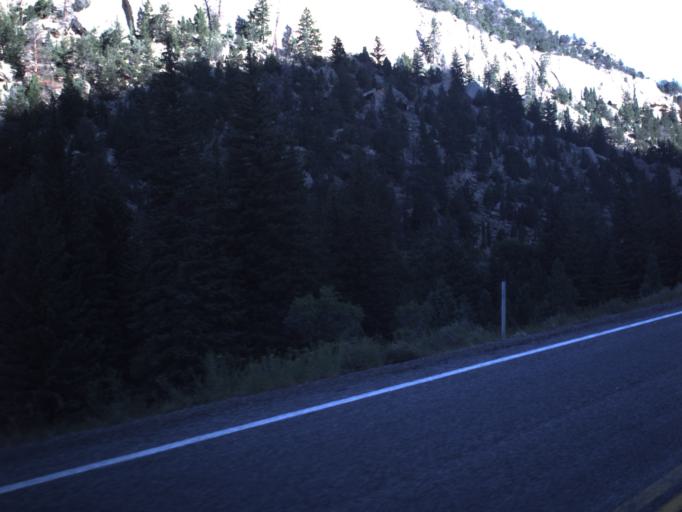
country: US
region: Utah
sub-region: Emery County
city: Huntington
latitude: 39.4273
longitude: -111.1297
